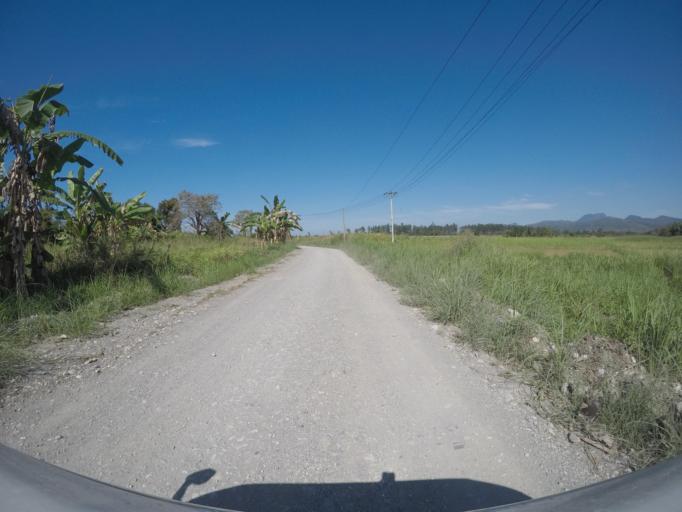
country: TL
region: Viqueque
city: Viqueque
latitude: -8.9393
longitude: 126.1156
